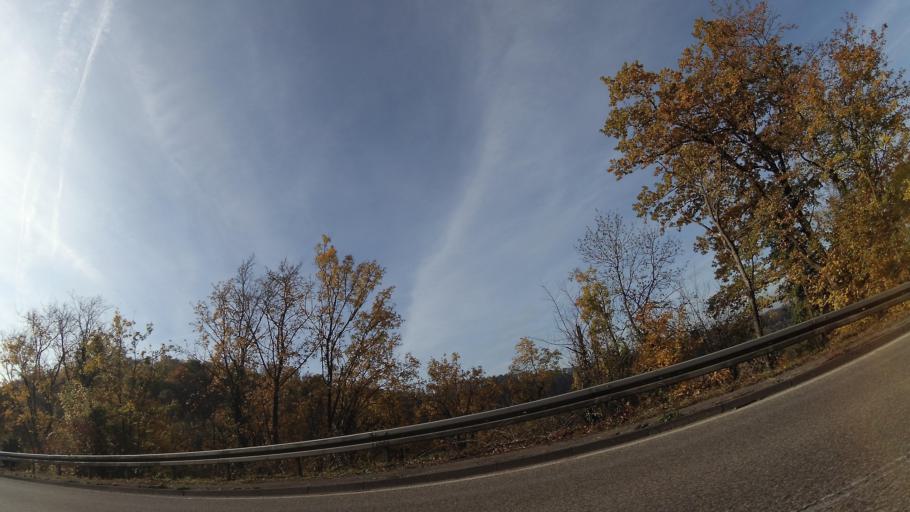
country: DE
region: Baden-Wuerttemberg
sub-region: Regierungsbezirk Stuttgart
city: Mockmuhl
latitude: 49.2912
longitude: 9.3303
